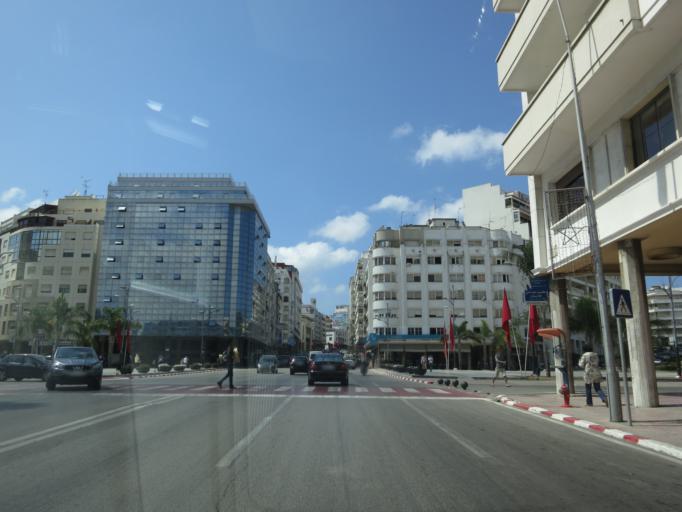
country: MA
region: Tanger-Tetouan
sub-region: Tanger-Assilah
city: Tangier
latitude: 35.7766
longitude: -5.8034
